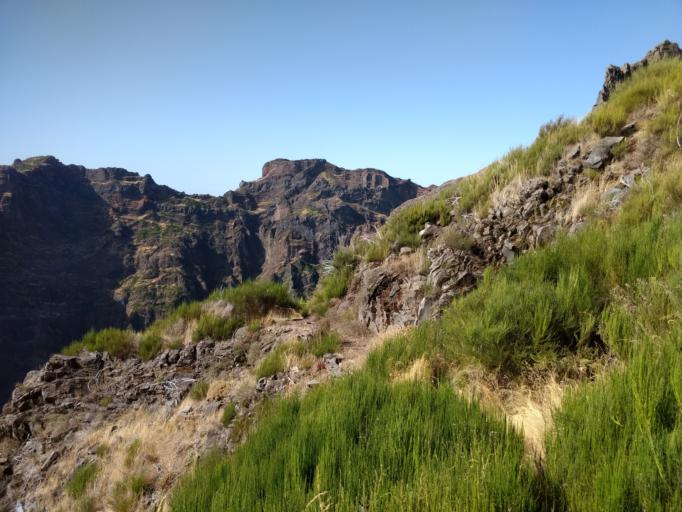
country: PT
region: Madeira
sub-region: Camara de Lobos
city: Curral das Freiras
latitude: 32.7480
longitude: -16.9338
